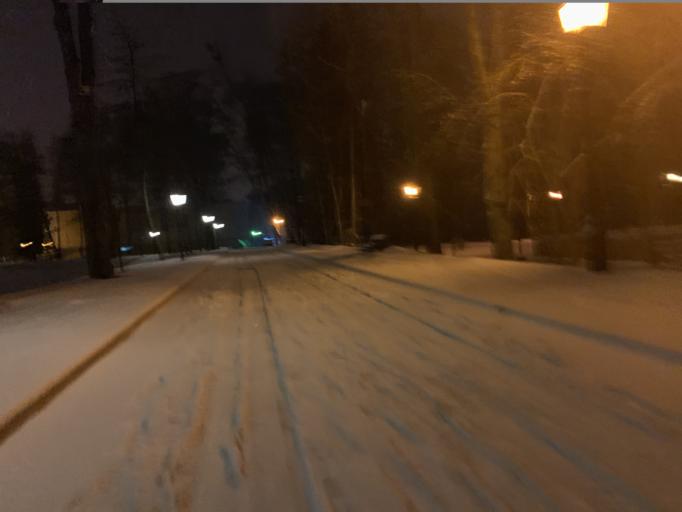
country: BY
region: Minsk
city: Nyasvizh
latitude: 53.2237
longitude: 26.6922
